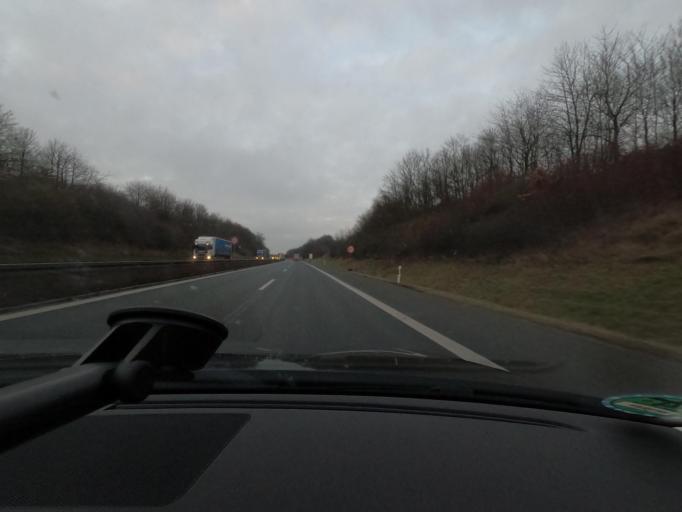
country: DE
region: Bavaria
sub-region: Upper Franconia
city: Hirschaid
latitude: 49.8346
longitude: 11.0056
